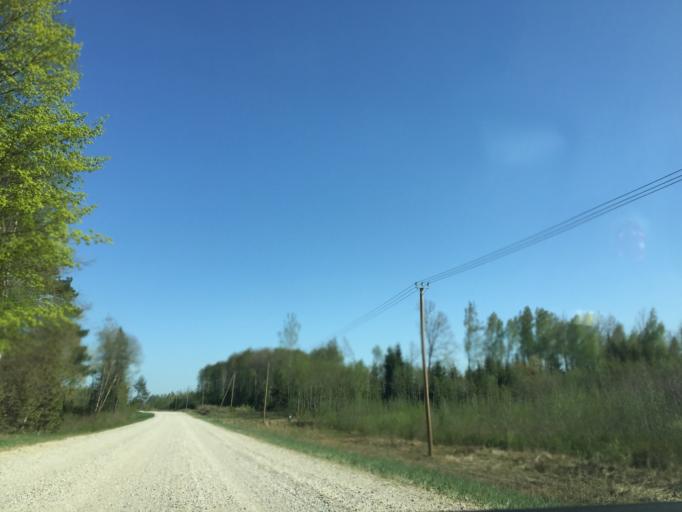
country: LV
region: Skriveri
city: Skriveri
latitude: 56.8396
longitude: 25.1039
